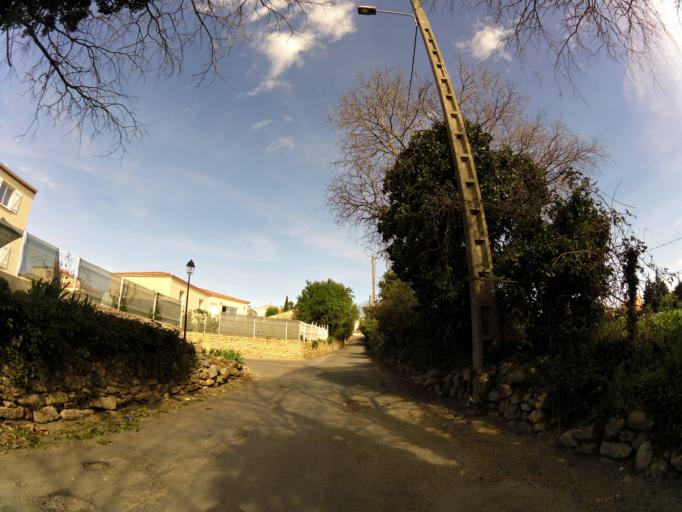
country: FR
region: Languedoc-Roussillon
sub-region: Departement du Gard
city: Mus
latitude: 43.7386
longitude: 4.1980
